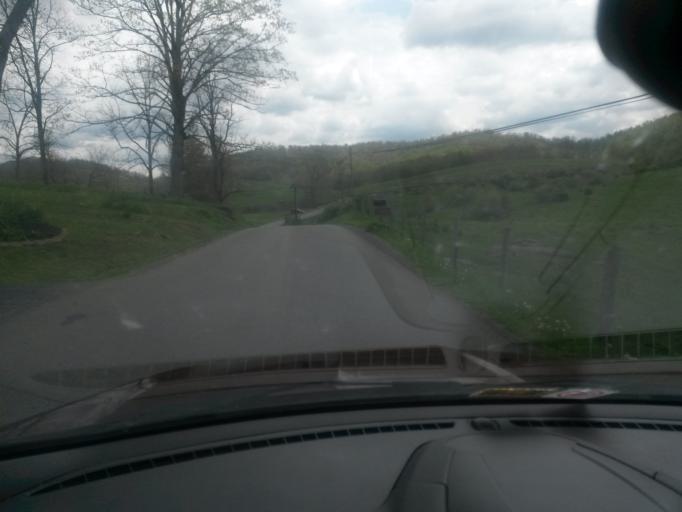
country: US
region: West Virginia
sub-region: Greenbrier County
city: White Sulphur Springs
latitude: 38.0351
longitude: -80.3333
